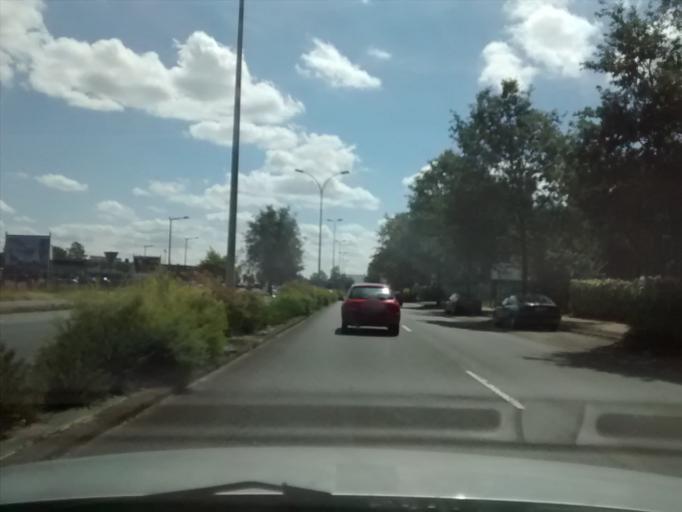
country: FR
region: Pays de la Loire
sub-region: Departement de la Sarthe
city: Le Mans
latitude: 47.9822
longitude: 0.1889
